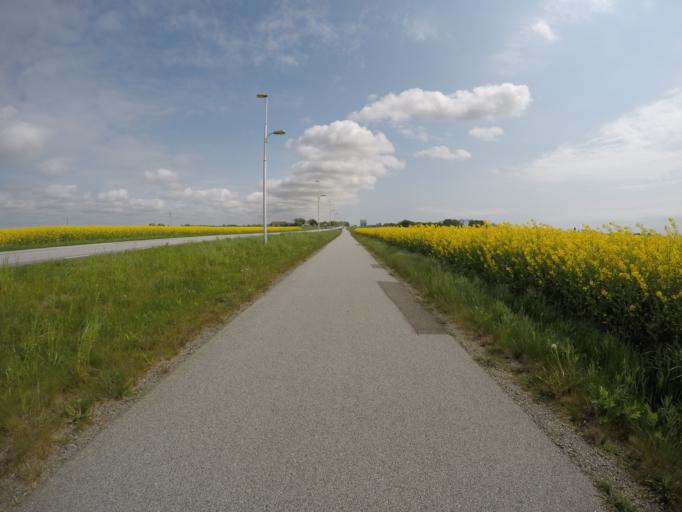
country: SE
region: Skane
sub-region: Malmo
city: Tygelsjo
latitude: 55.5356
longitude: 12.9875
